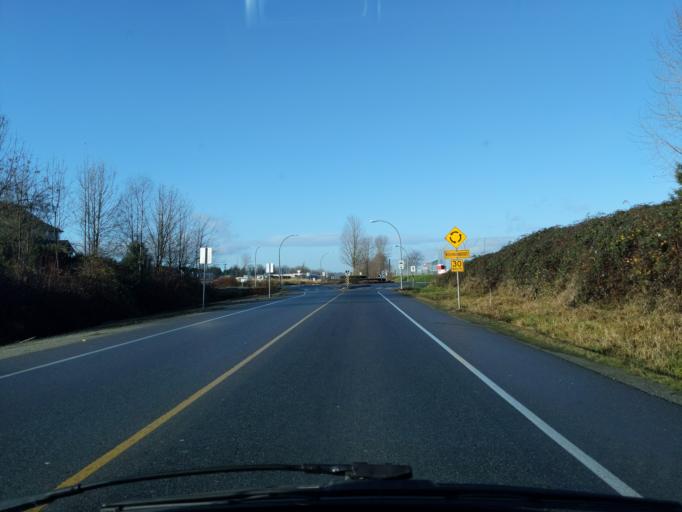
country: CA
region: British Columbia
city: Pitt Meadows
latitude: 49.2084
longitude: -122.6770
